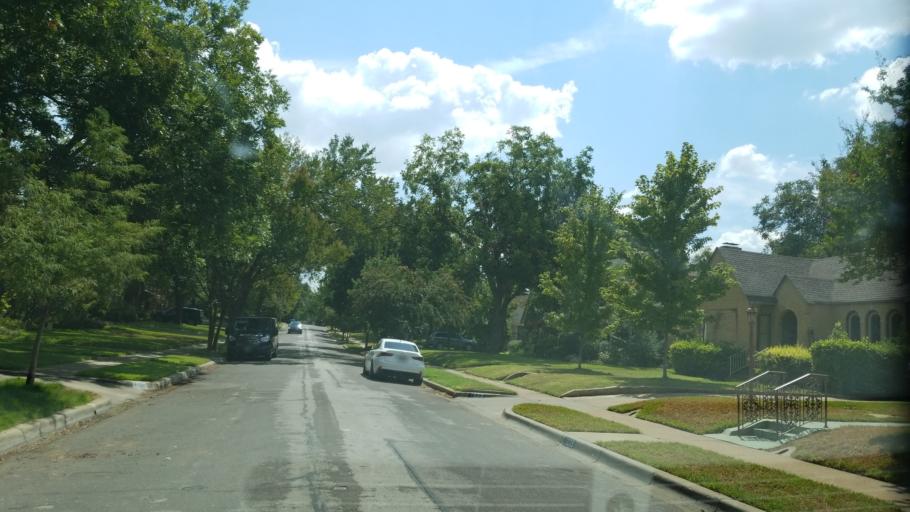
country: US
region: Texas
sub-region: Dallas County
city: Dallas
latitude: 32.7567
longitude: -96.8403
